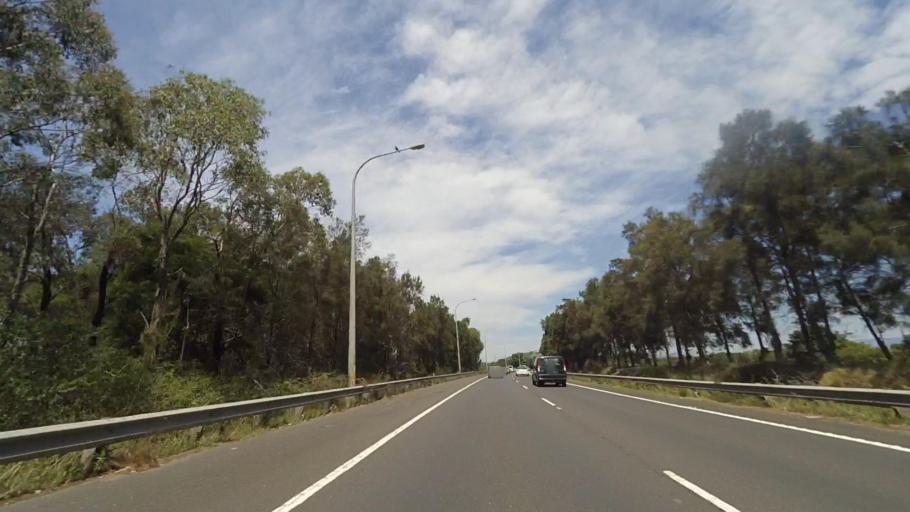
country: AU
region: New South Wales
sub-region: Wollongong
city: Mount Saint Thomas
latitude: -34.4525
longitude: 150.8593
